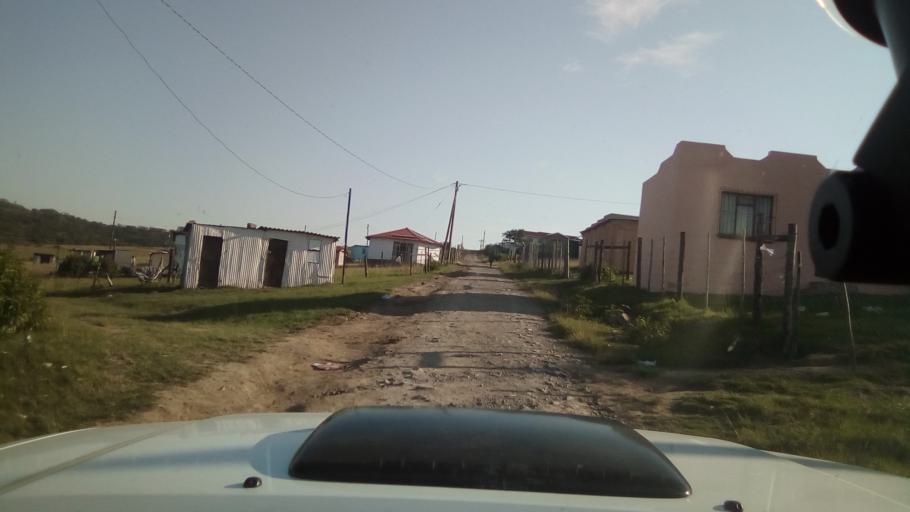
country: ZA
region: Eastern Cape
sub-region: Buffalo City Metropolitan Municipality
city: East London
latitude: -32.8479
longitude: 27.9870
